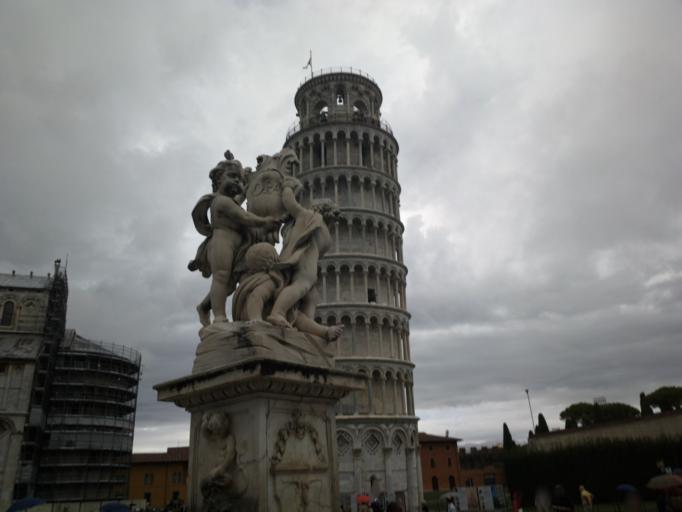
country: IT
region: Tuscany
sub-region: Province of Pisa
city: Pisa
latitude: 43.7225
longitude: 10.3963
